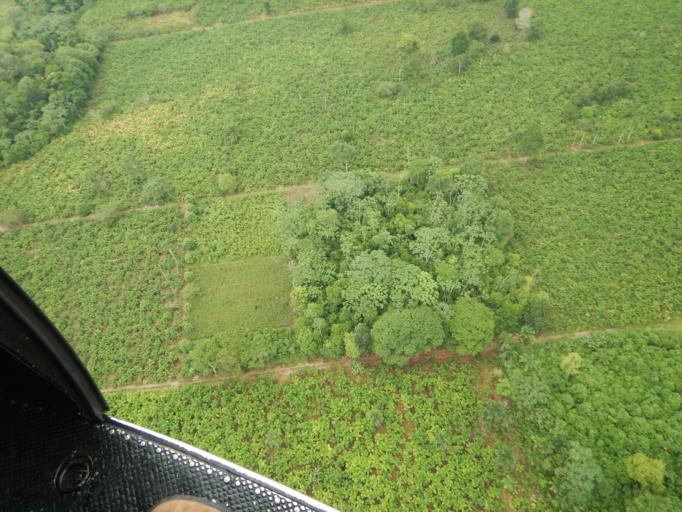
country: BO
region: Cochabamba
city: Chimore
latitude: -17.2377
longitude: -64.6845
